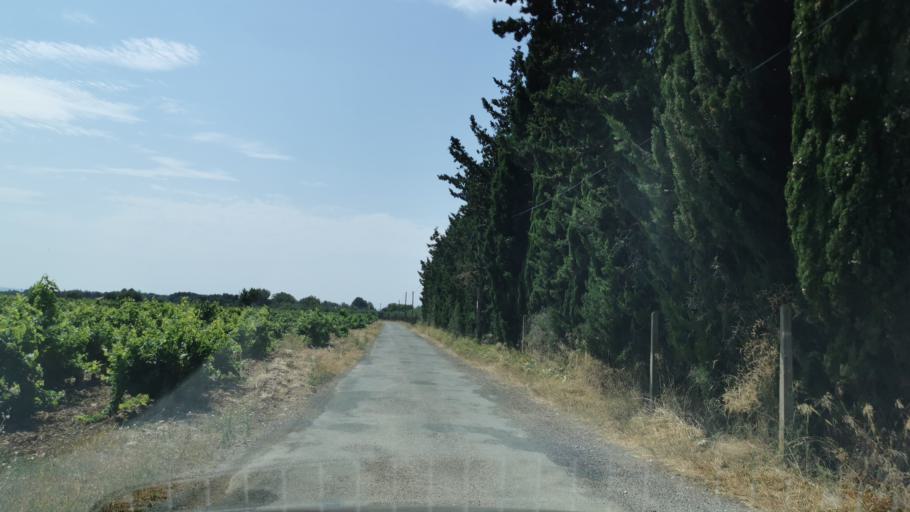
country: FR
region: Languedoc-Roussillon
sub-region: Departement de l'Aude
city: Bize-Minervois
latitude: 43.3003
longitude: 2.8751
